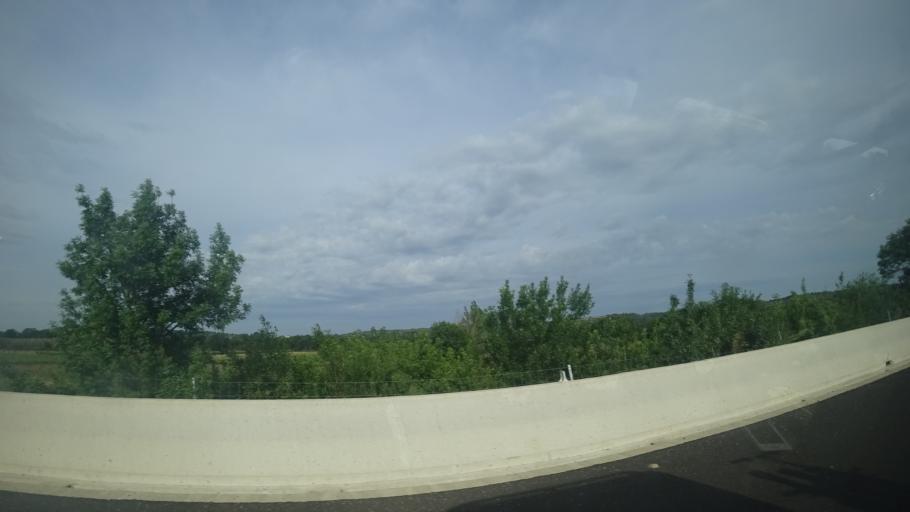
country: FR
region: Languedoc-Roussillon
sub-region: Departement de l'Herault
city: Pezenas
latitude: 43.4602
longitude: 3.4321
